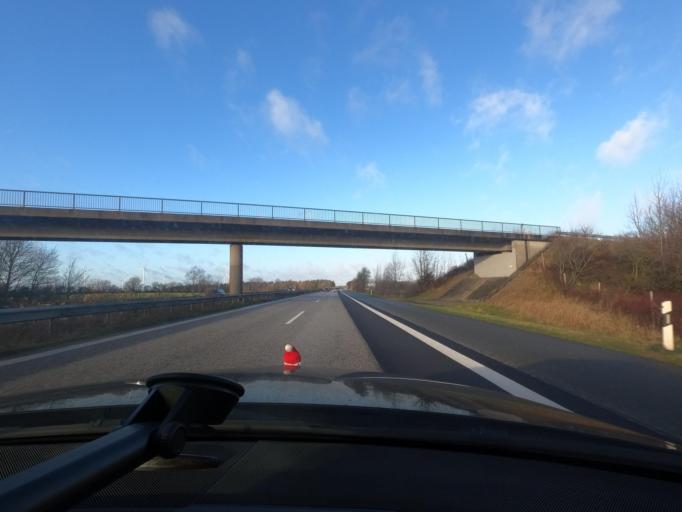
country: DE
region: Schleswig-Holstein
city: Bollingstedt
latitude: 54.6031
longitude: 9.4513
